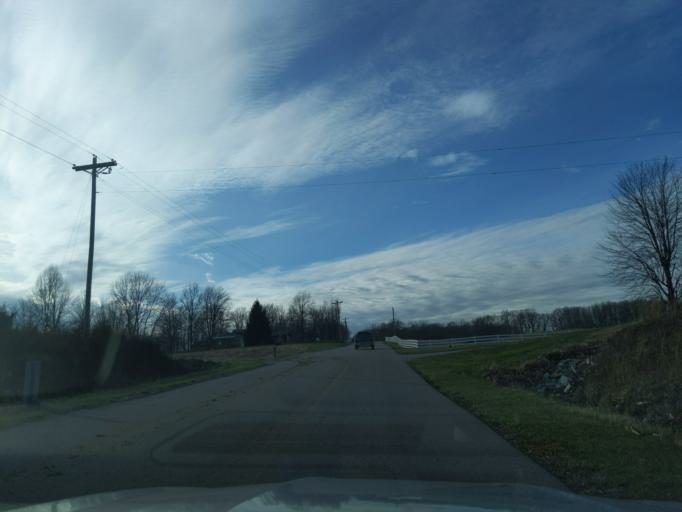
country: US
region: Indiana
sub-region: Decatur County
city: Westport
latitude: 39.1908
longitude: -85.5395
